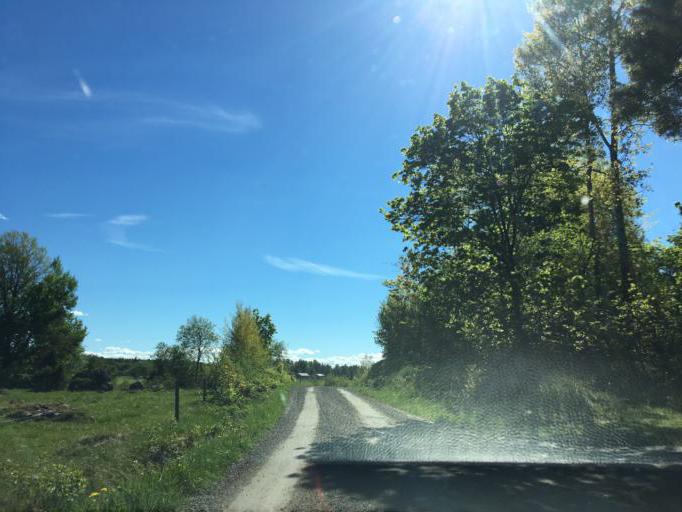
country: SE
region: Soedermanland
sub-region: Eskilstuna Kommun
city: Kvicksund
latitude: 59.3445
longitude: 16.3063
